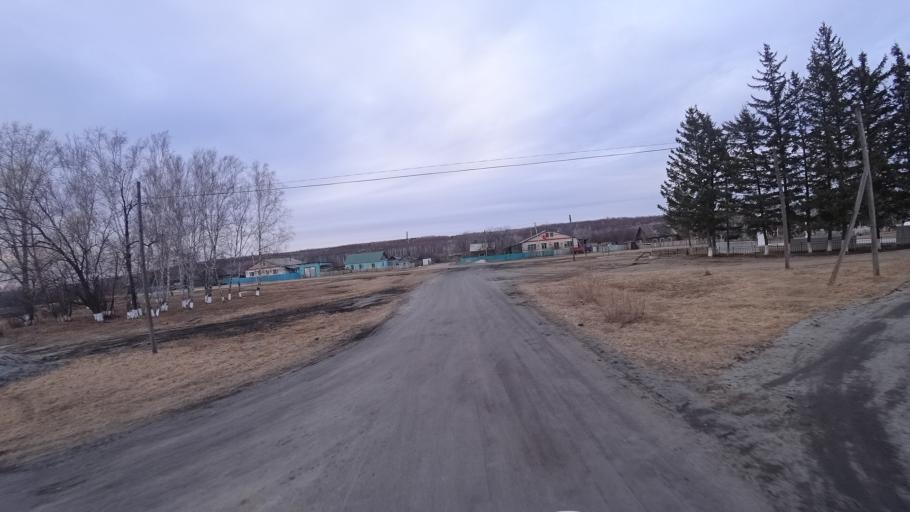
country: RU
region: Amur
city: Bureya
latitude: 50.0193
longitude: 129.7704
